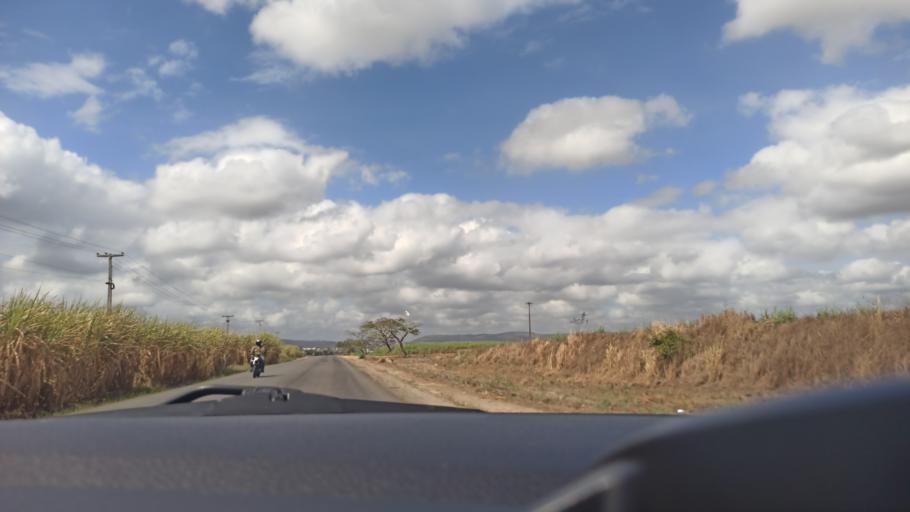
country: BR
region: Pernambuco
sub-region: Timbauba
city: Timbauba
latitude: -7.4870
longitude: -35.2934
